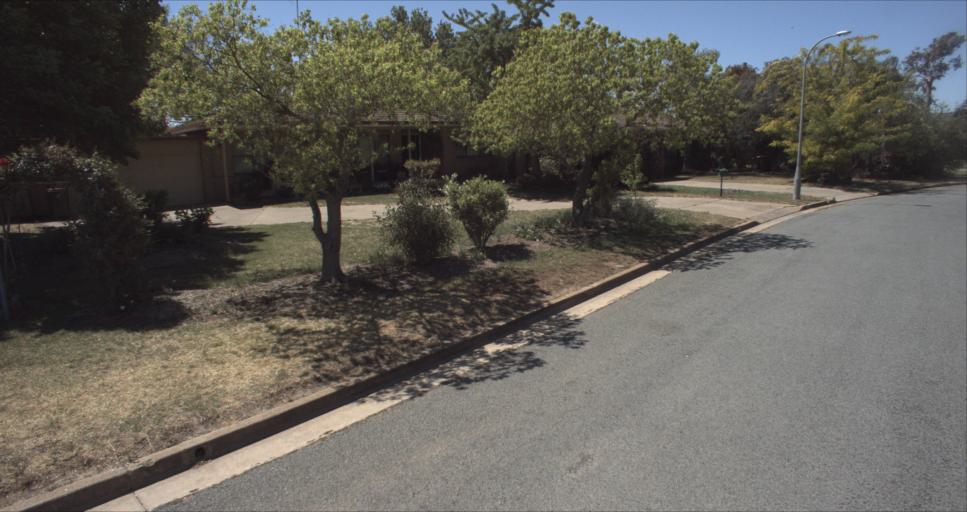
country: AU
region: New South Wales
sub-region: Leeton
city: Leeton
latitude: -34.5459
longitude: 146.4005
